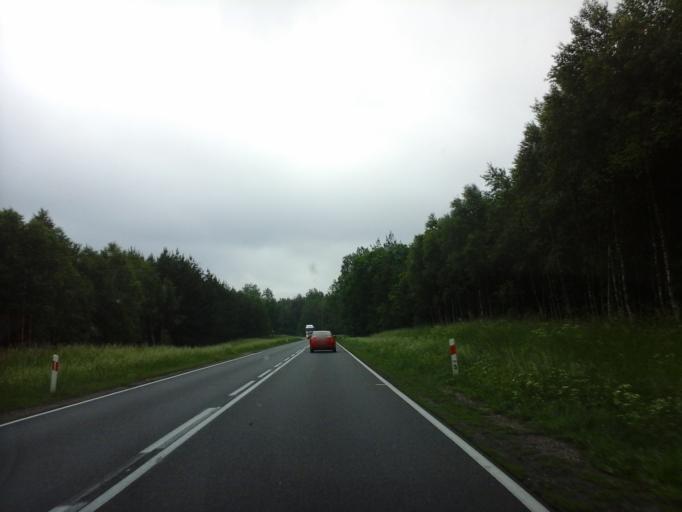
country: PL
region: West Pomeranian Voivodeship
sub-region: Powiat walecki
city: Miroslawiec
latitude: 53.3330
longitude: 16.0603
